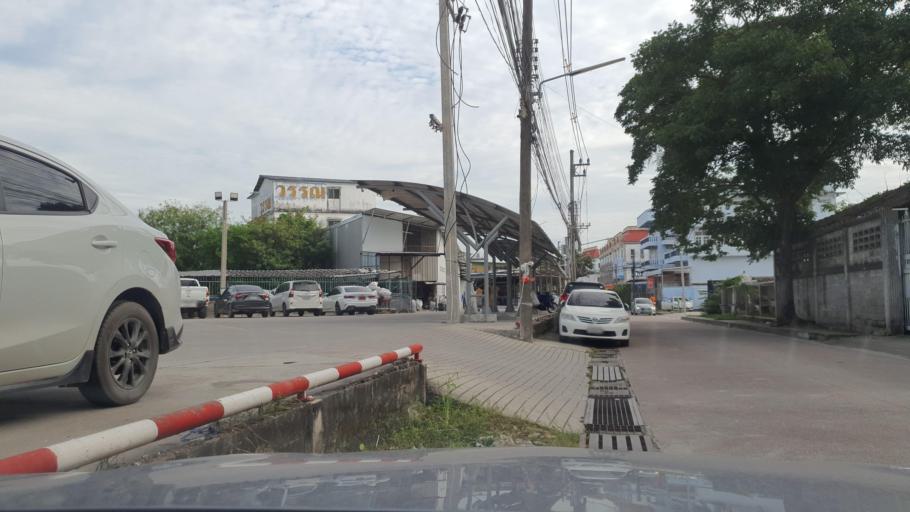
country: TH
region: Rayong
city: Rayong
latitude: 12.6858
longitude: 101.2736
